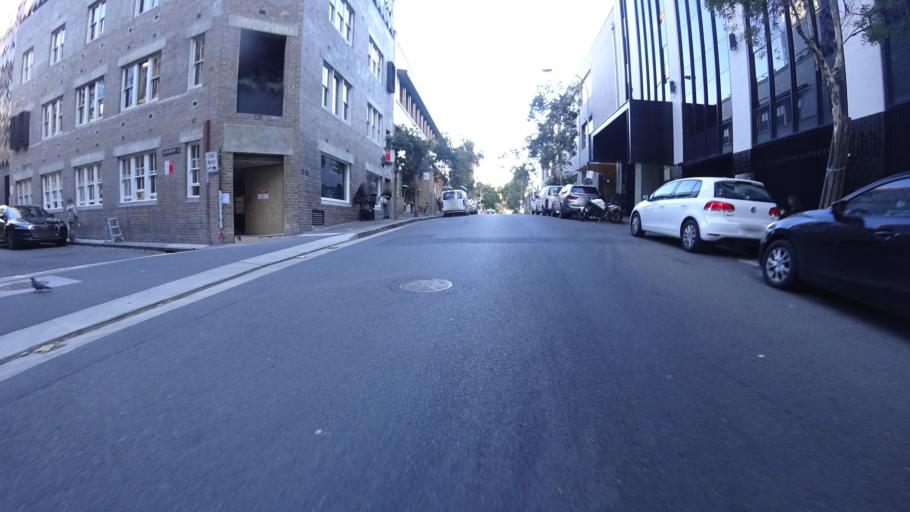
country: AU
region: New South Wales
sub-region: City of Sydney
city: Haymarket
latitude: -33.8790
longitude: 151.2110
